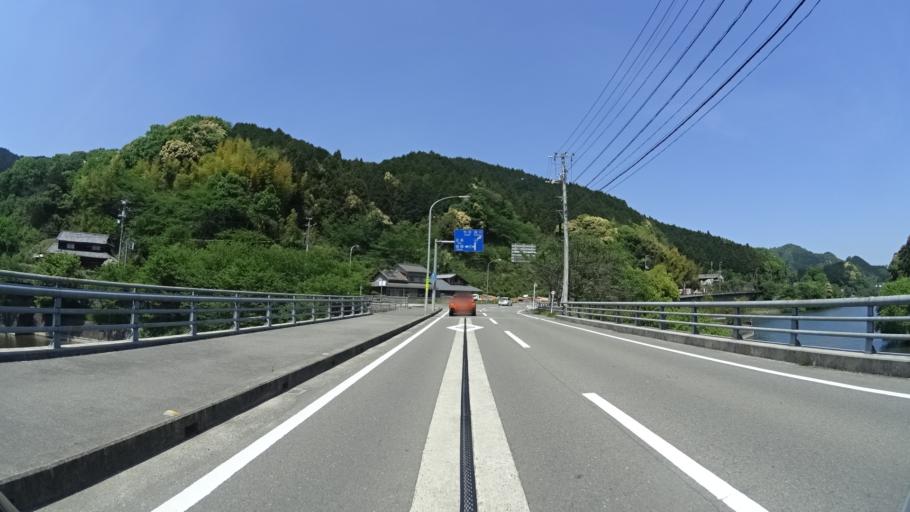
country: JP
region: Ehime
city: Hojo
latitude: 33.9931
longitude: 132.9150
